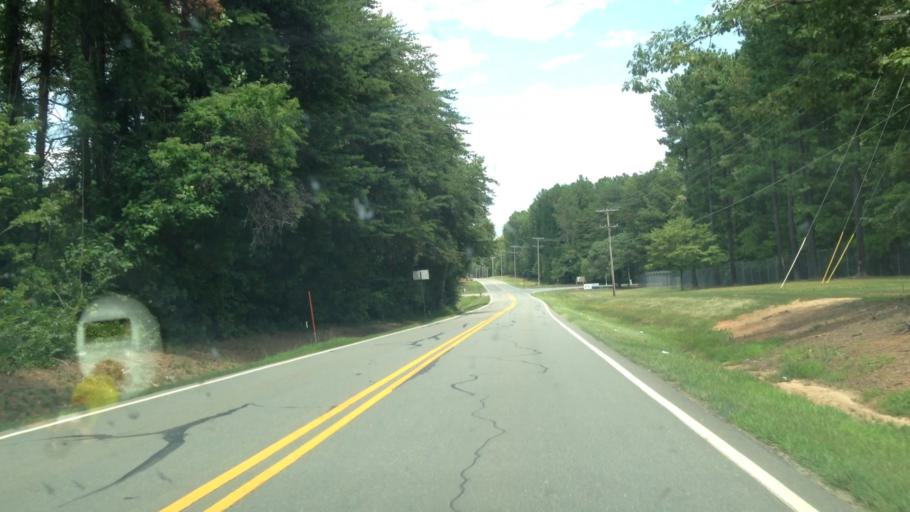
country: US
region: North Carolina
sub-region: Stokes County
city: Walnut Cove
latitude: 36.2884
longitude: -80.0666
